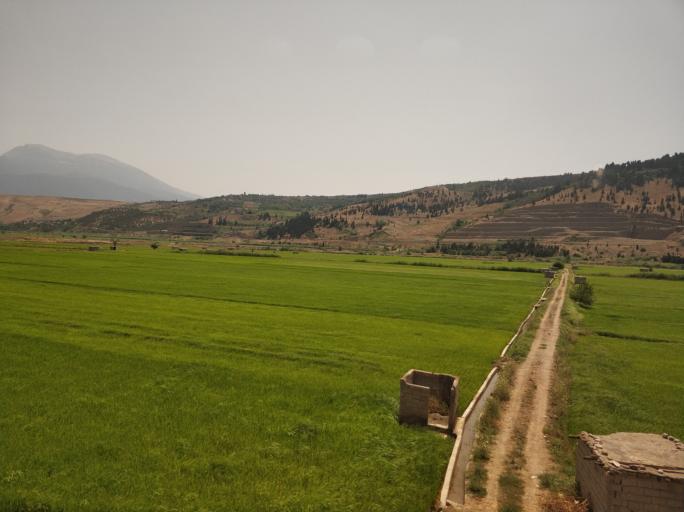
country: IR
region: Gilan
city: Pa'in-e Bazar-e Rudbar
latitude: 36.8699
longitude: 49.4913
